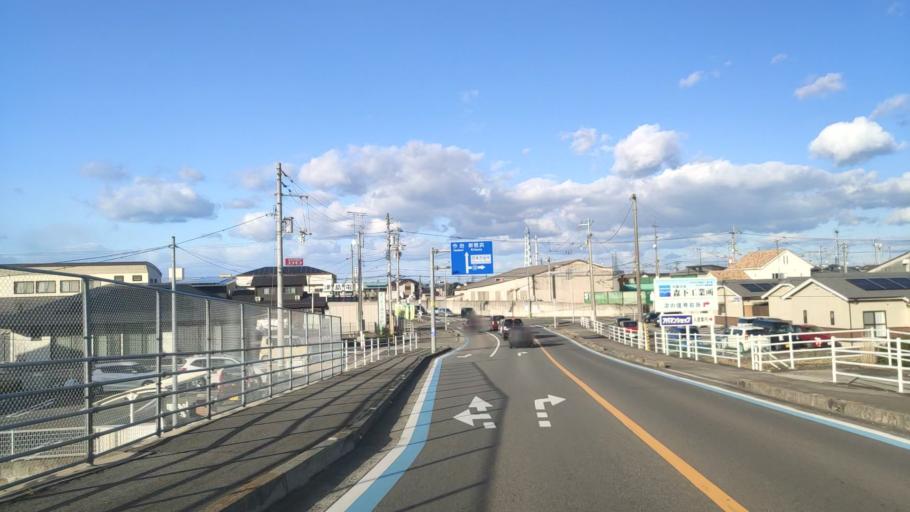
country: JP
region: Ehime
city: Saijo
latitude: 33.9144
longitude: 133.1621
